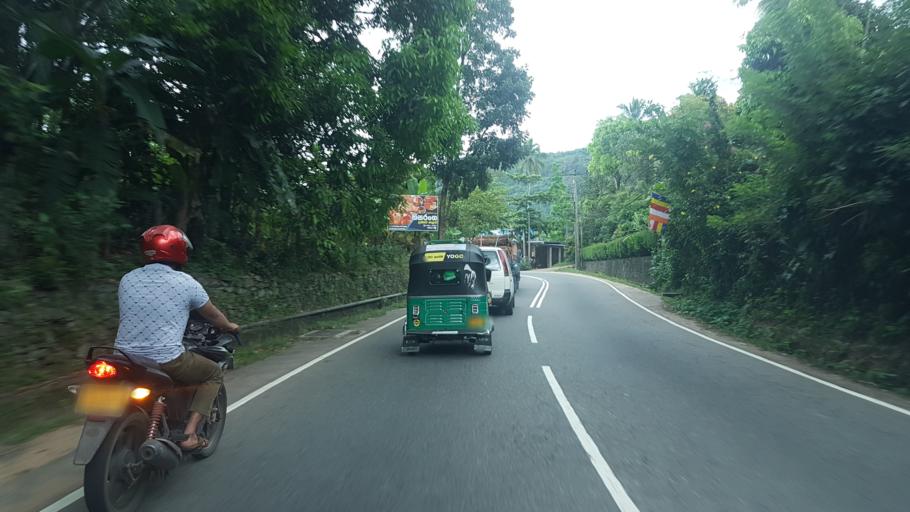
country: LK
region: Western
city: Hanwella Ihala
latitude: 7.0119
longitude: 80.2629
